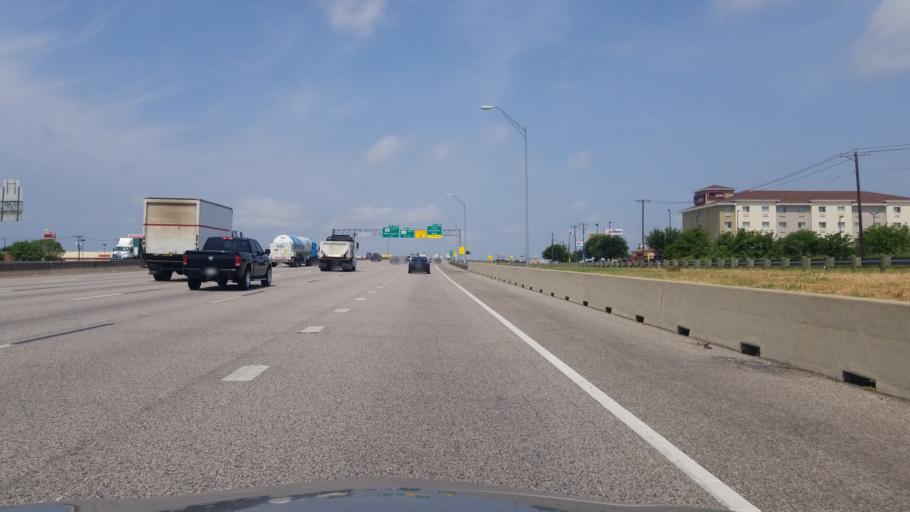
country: US
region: Texas
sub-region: Dallas County
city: Grand Prairie
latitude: 32.6763
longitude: -97.0380
